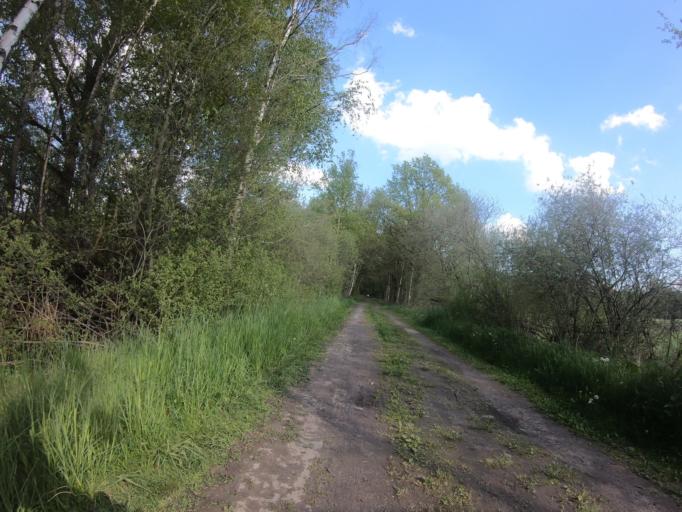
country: DE
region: Lower Saxony
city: Sassenburg
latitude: 52.5296
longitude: 10.6180
